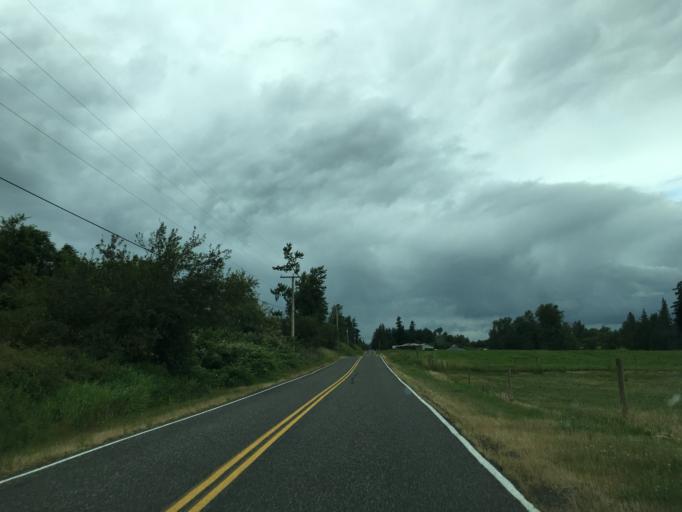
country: US
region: Washington
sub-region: Whatcom County
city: Nooksack
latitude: 48.9820
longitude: -122.3357
